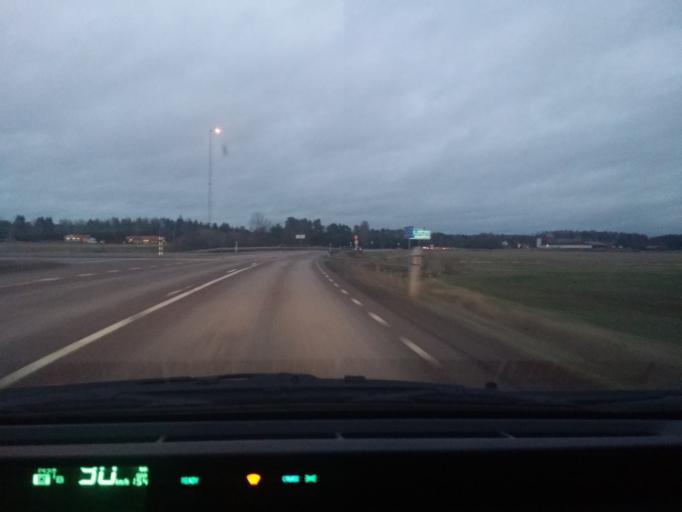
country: SE
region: Vaestmanland
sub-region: Hallstahammars Kommun
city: Kolback
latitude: 59.5569
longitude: 16.3394
